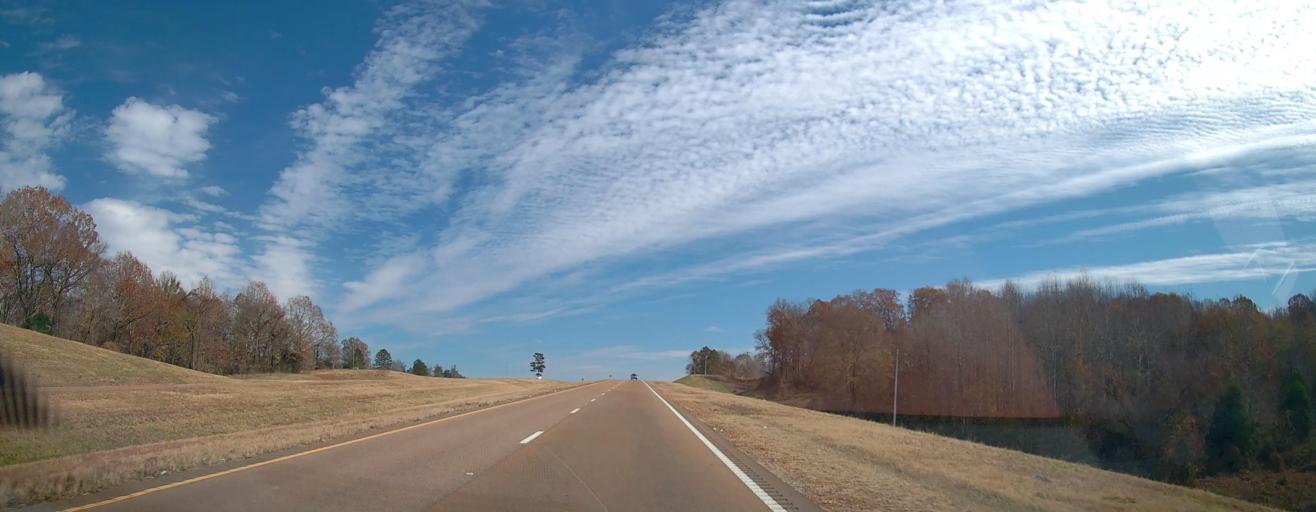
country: US
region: Mississippi
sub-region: Benton County
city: Ashland
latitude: 34.9459
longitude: -89.1875
